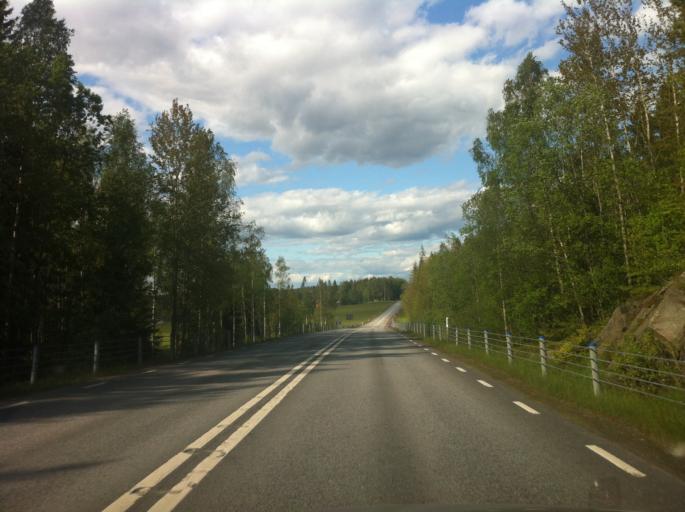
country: SE
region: Vaermland
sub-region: Storfors Kommun
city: Storfors
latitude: 59.4468
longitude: 14.2385
